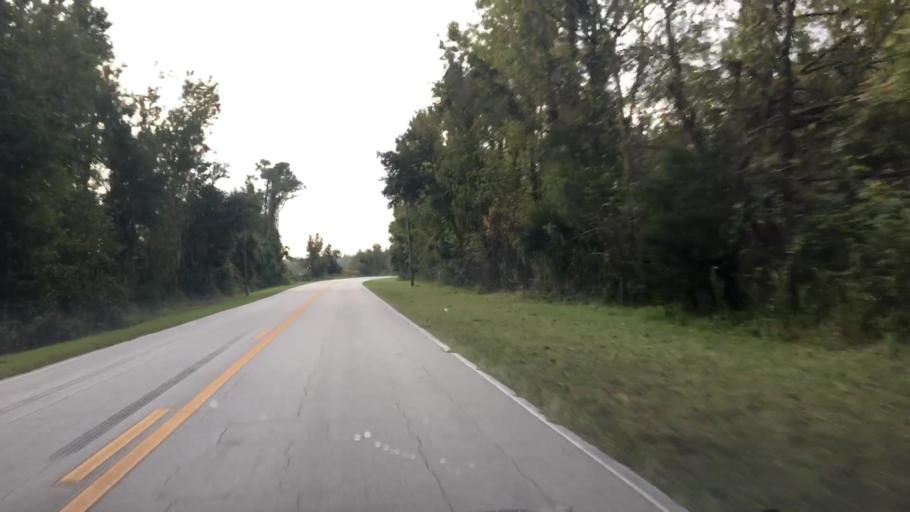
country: US
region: Florida
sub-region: Seminole County
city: Midway
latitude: 28.8414
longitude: -81.1961
